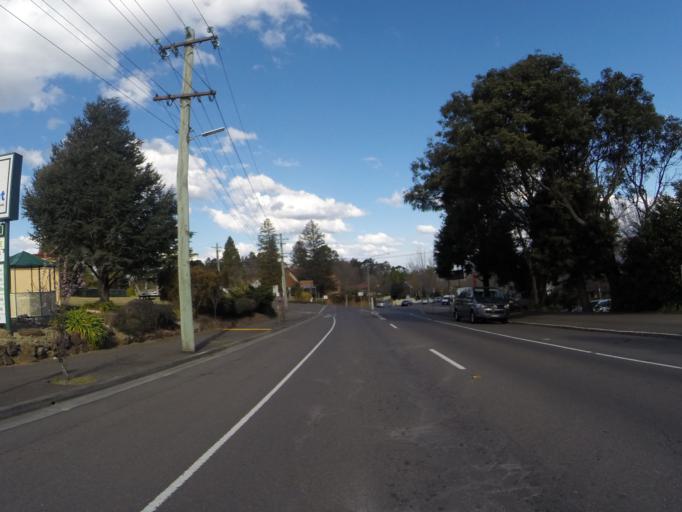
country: AU
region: New South Wales
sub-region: Blue Mountains Municipality
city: Katoomba
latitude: -33.7295
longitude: 150.3115
